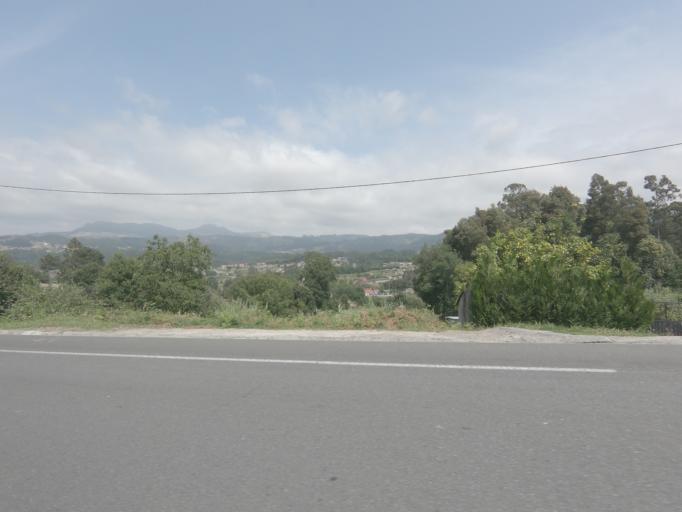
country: ES
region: Galicia
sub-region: Provincia de Pontevedra
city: Gondomar
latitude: 42.0988
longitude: -8.7595
